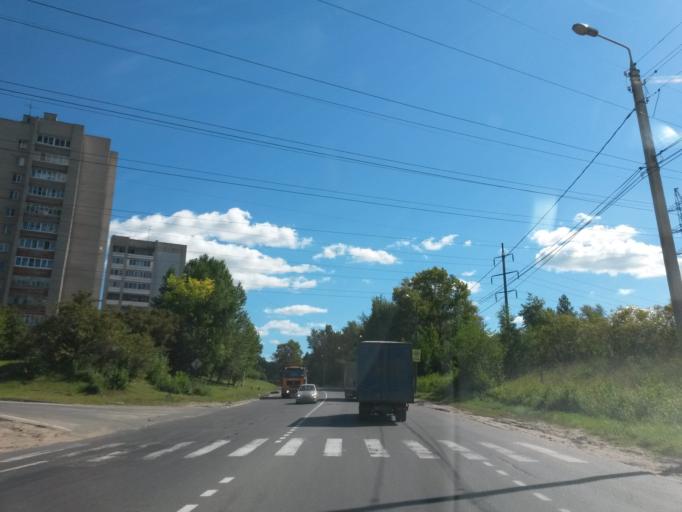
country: RU
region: Jaroslavl
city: Yaroslavl
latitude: 57.5855
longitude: 39.8219
